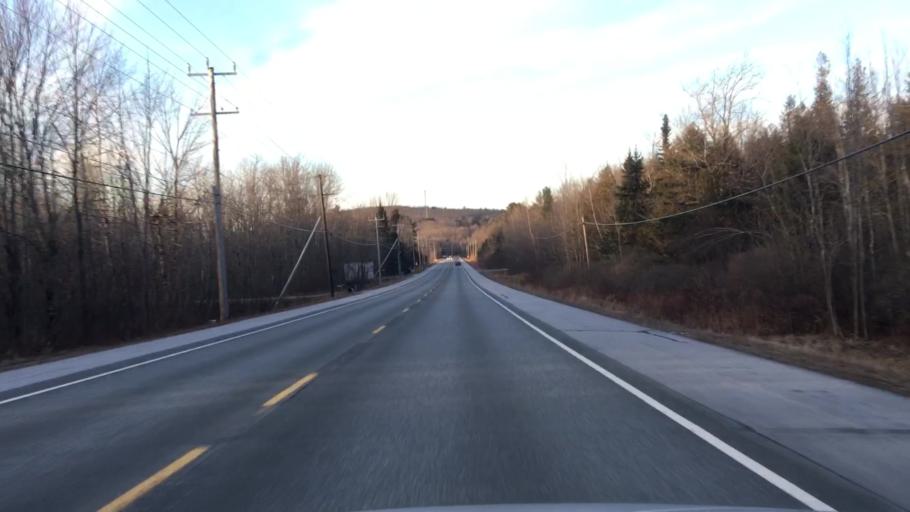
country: US
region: Maine
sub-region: Hancock County
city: Dedham
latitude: 44.7073
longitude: -68.6010
